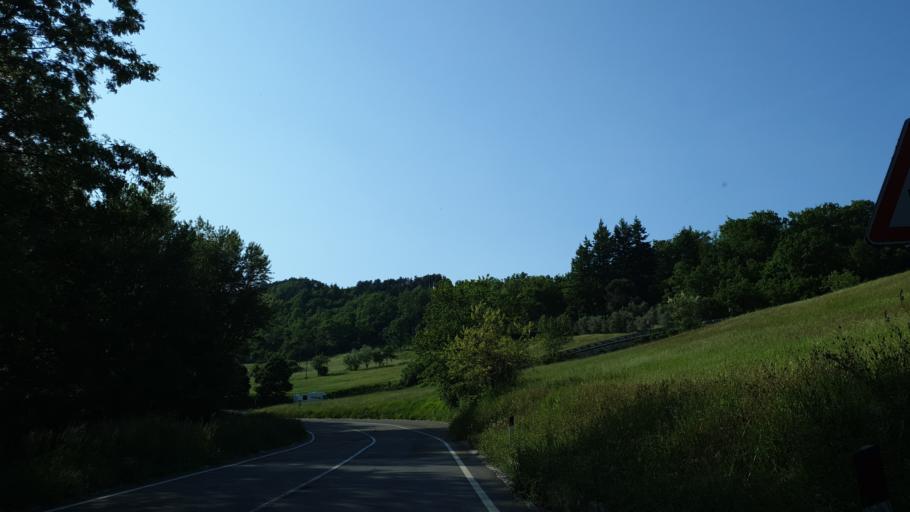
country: IT
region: Tuscany
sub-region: Province of Arezzo
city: Castel San Niccolo
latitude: 43.7715
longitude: 11.6946
